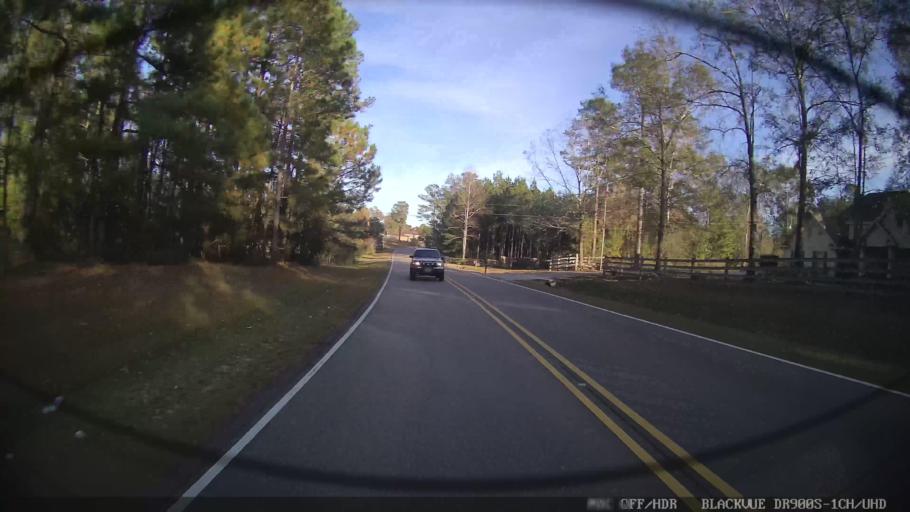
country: US
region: Mississippi
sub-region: Lamar County
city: Purvis
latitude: 31.1378
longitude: -89.3639
